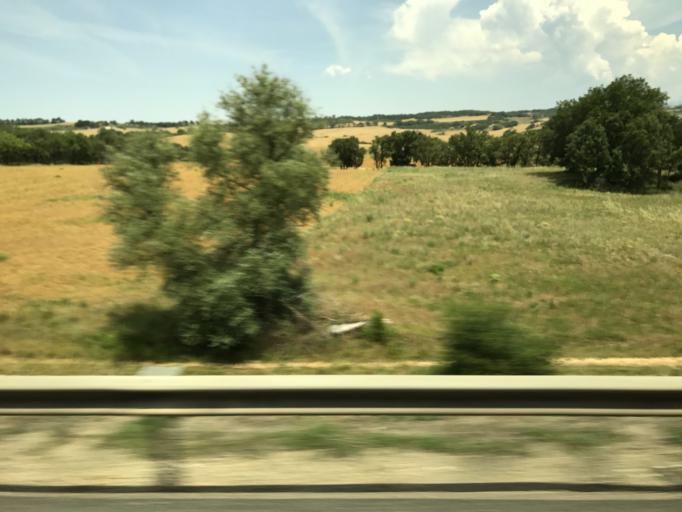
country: ES
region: Castille and Leon
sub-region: Provincia de Burgos
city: Saldana de Burgos
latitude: 42.2767
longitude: -3.7033
